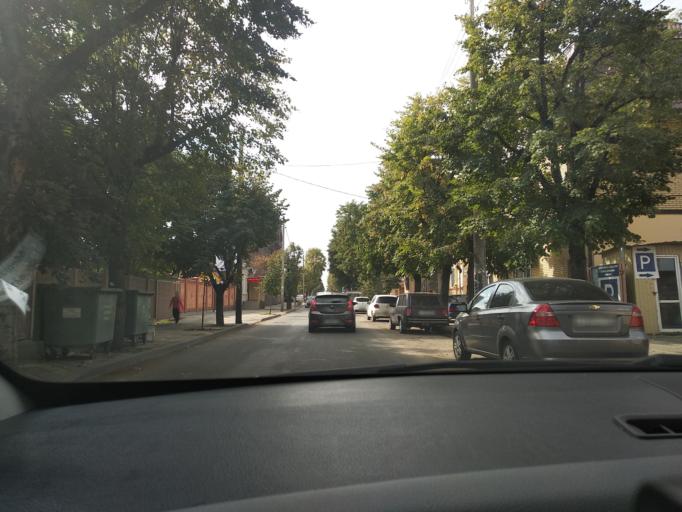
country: RU
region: Krasnodarskiy
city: Krasnodar
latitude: 45.0315
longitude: 38.9795
